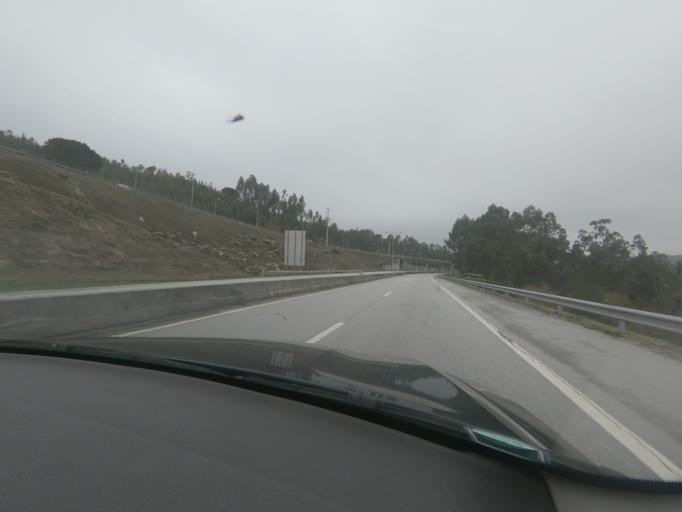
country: PT
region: Viseu
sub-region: Viseu
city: Viseu
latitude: 40.6053
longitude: -7.9737
